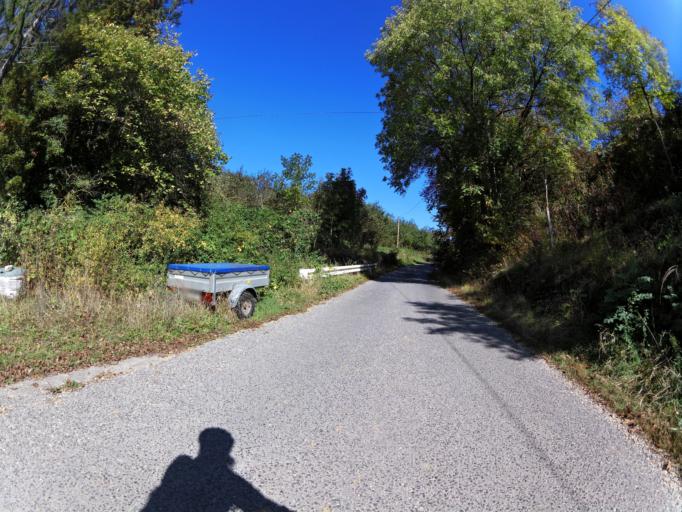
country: DE
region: Bavaria
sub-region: Regierungsbezirk Unterfranken
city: Ochsenfurt
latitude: 49.6759
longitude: 10.0539
